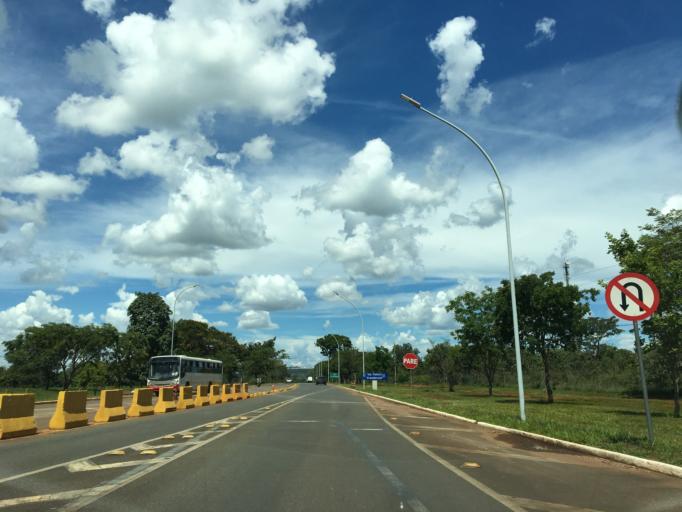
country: BR
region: Federal District
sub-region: Brasilia
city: Brasilia
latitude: -15.8015
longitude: -47.8482
